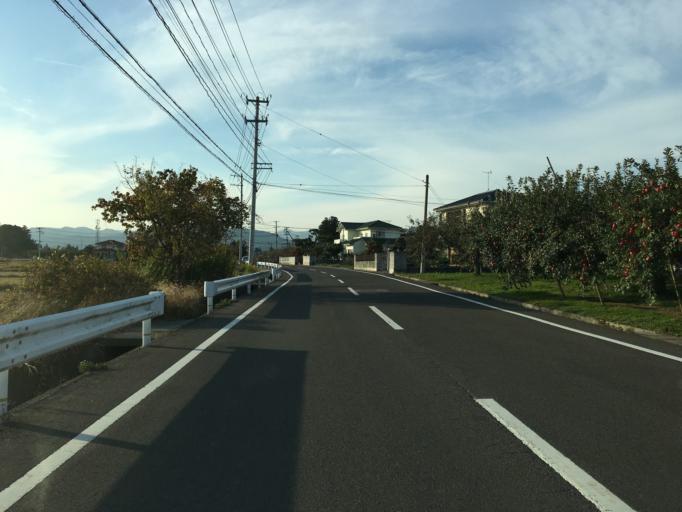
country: JP
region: Fukushima
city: Fukushima-shi
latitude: 37.8043
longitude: 140.4683
